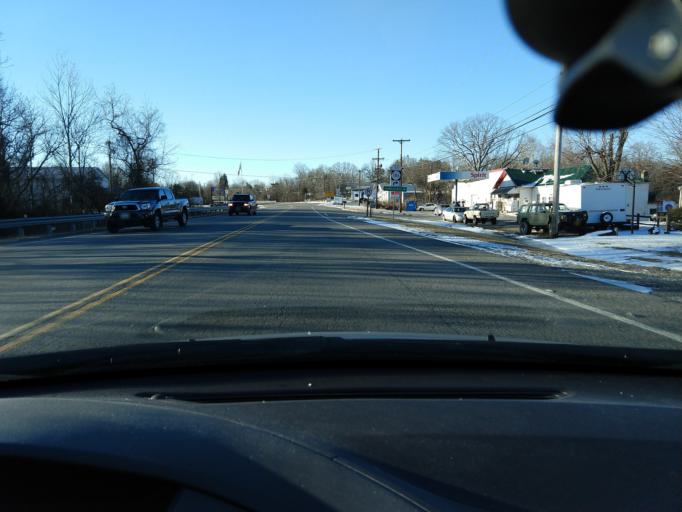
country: US
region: Virginia
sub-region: City of Bedford
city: Bedford
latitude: 37.3161
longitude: -79.5373
